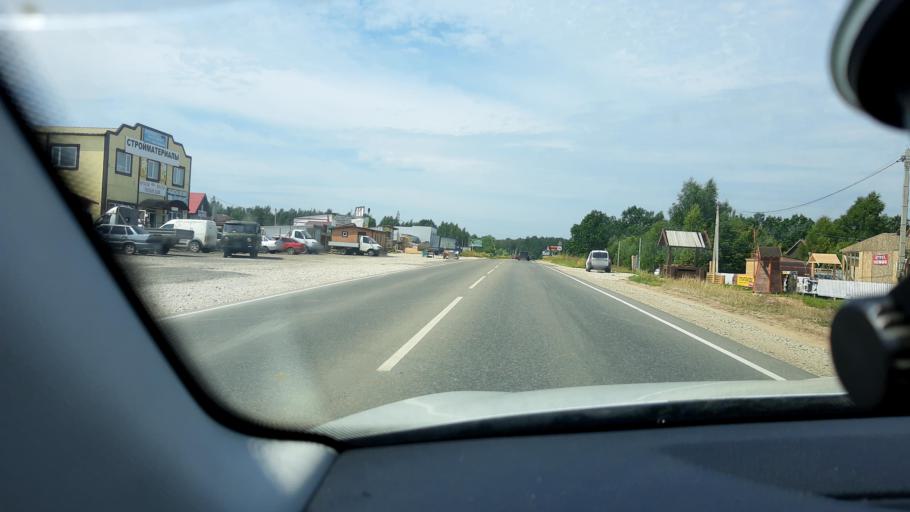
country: RU
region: Tula
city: Zaokskiy
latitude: 54.7454
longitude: 37.4125
